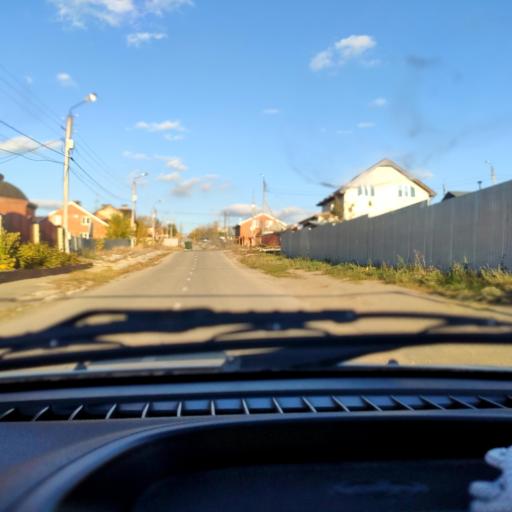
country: RU
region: Samara
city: Zhigulevsk
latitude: 53.4873
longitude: 49.5239
